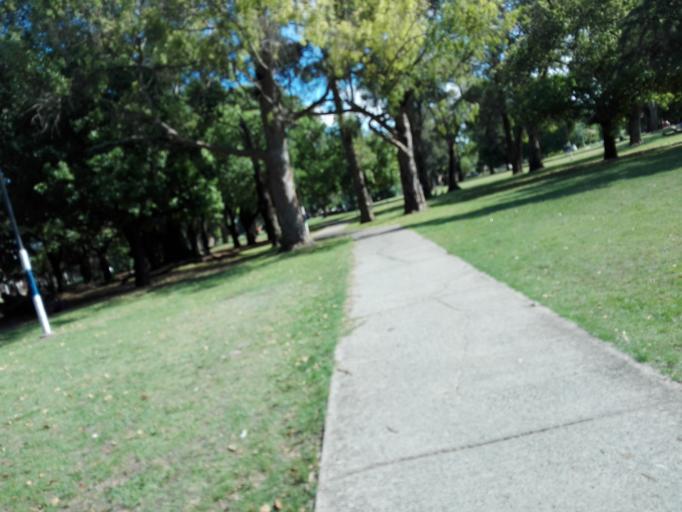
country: AR
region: Buenos Aires
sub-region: Partido de La Plata
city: La Plata
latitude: -34.9333
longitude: -57.9682
